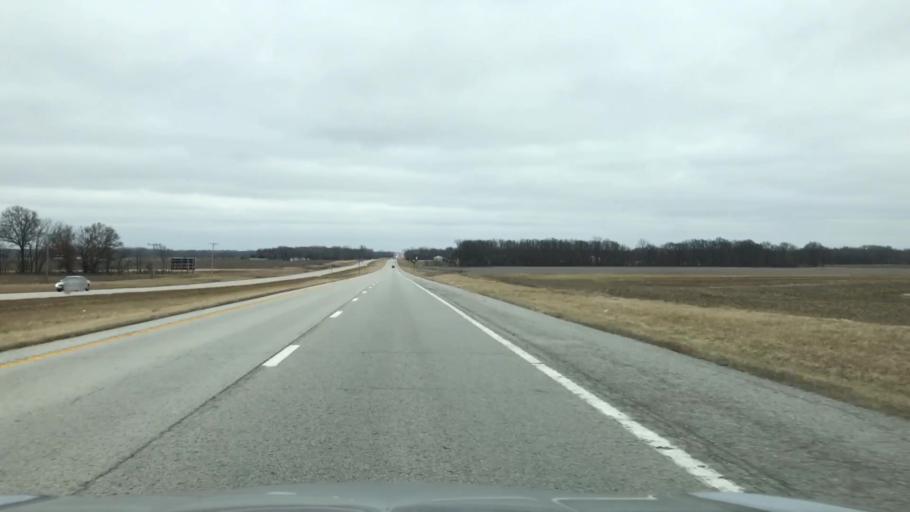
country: US
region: Missouri
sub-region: Livingston County
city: Chillicothe
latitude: 39.7764
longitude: -93.4565
